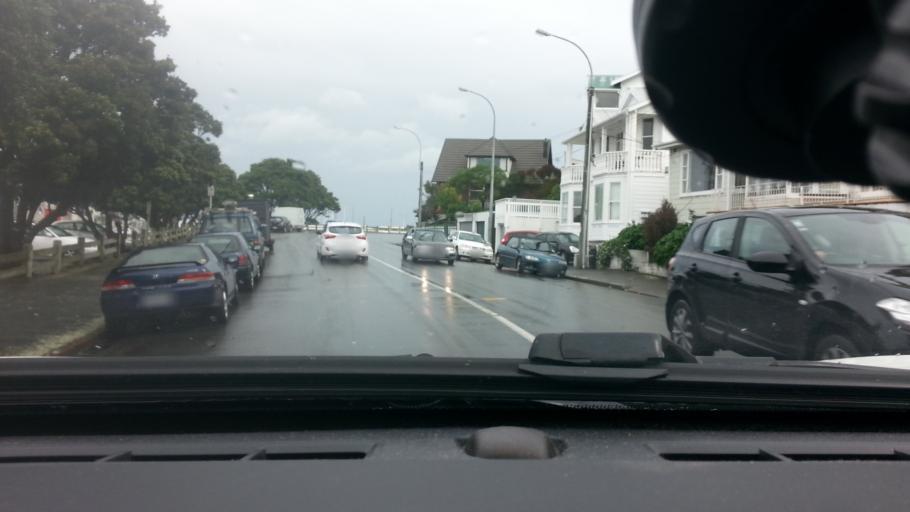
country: NZ
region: Wellington
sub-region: Wellington City
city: Wellington
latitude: -41.3097
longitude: 174.7977
